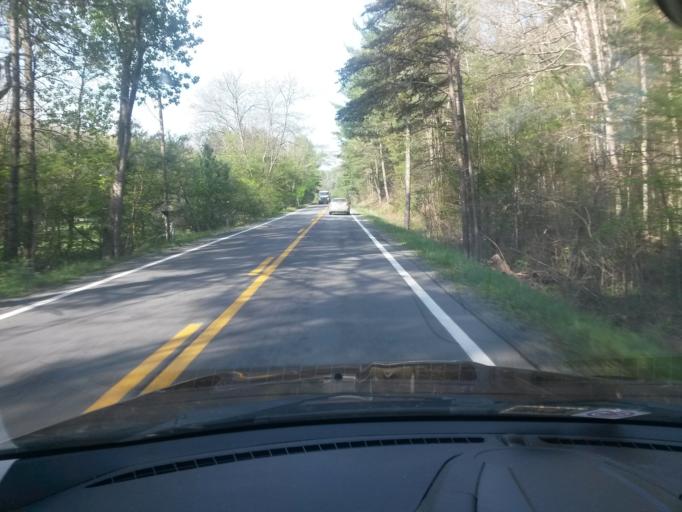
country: US
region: West Virginia
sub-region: Pocahontas County
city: Marlinton
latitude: 38.0817
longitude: -79.9921
